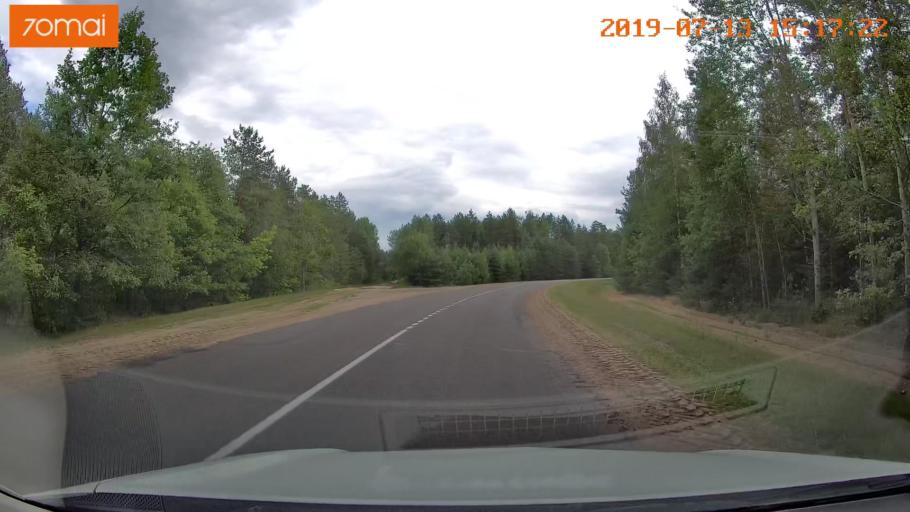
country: BY
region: Mogilev
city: Hlusha
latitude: 53.0968
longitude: 28.8438
